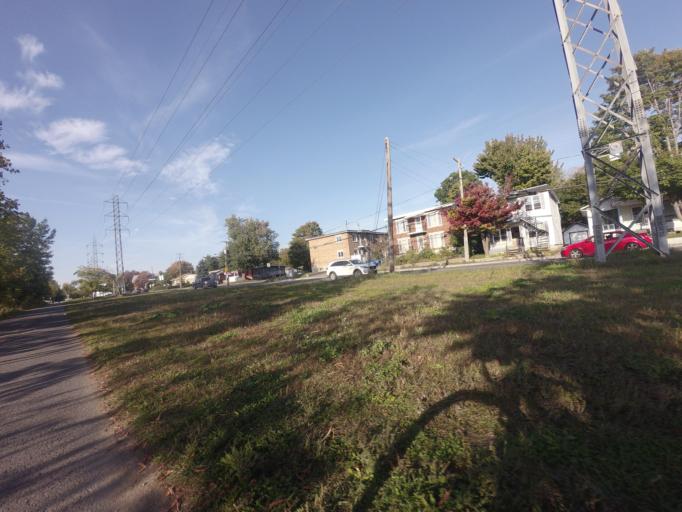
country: CA
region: Quebec
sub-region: Laurentides
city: Saint-Jerome
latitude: 45.7860
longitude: -73.9966
